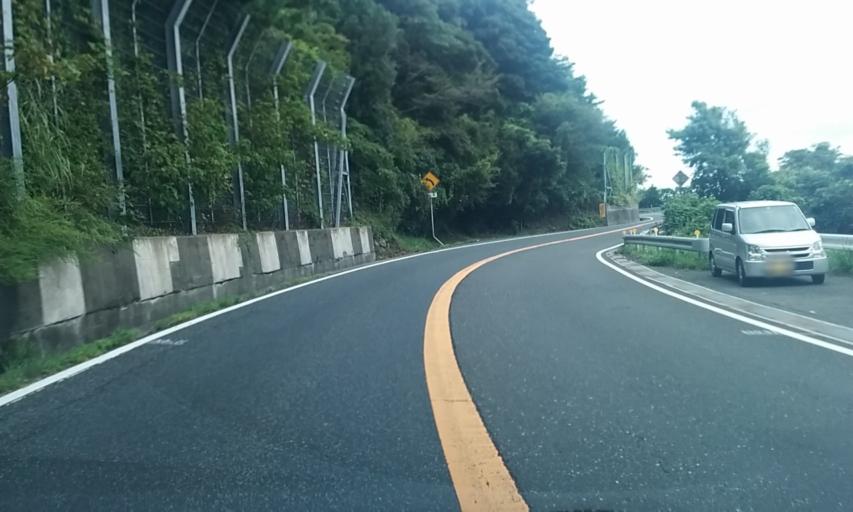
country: JP
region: Kyoto
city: Miyazu
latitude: 35.5315
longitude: 135.2690
